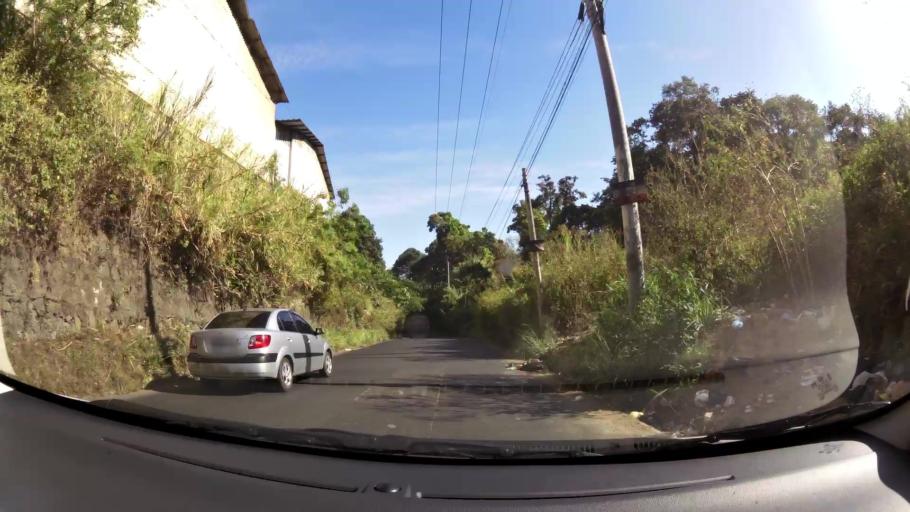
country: SV
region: Santa Ana
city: Santa Ana
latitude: 13.9818
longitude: -89.5835
